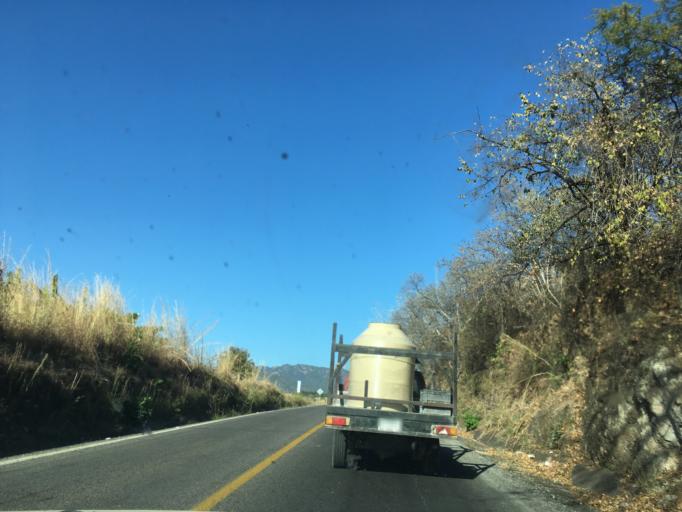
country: MX
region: Michoacan
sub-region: Gabriel Zamora
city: Lombardia
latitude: 19.1894
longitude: -102.0614
